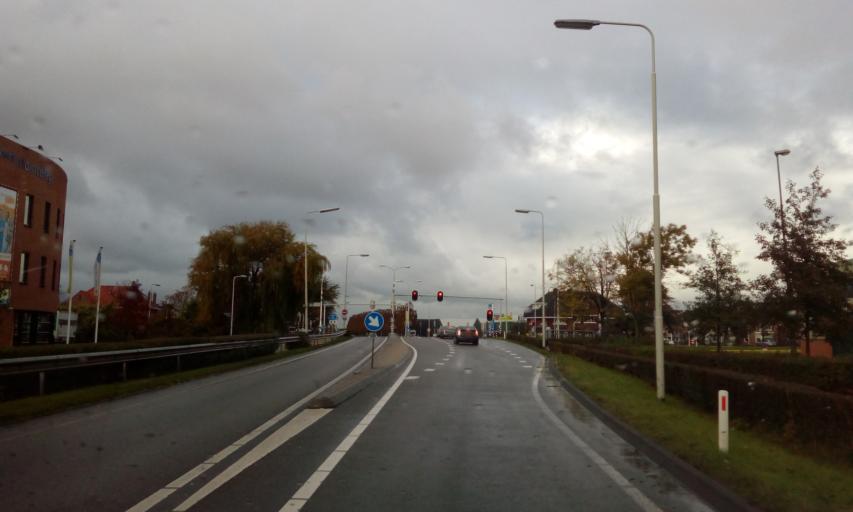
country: NL
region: South Holland
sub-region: Gemeente Westland
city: Honselersdijk
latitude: 52.0004
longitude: 4.2196
